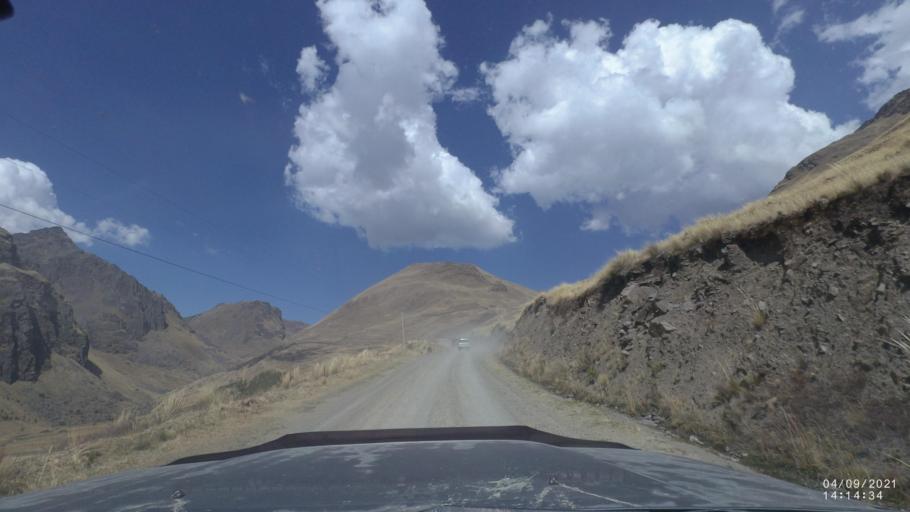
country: BO
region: Cochabamba
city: Sipe Sipe
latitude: -17.2264
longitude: -66.4440
